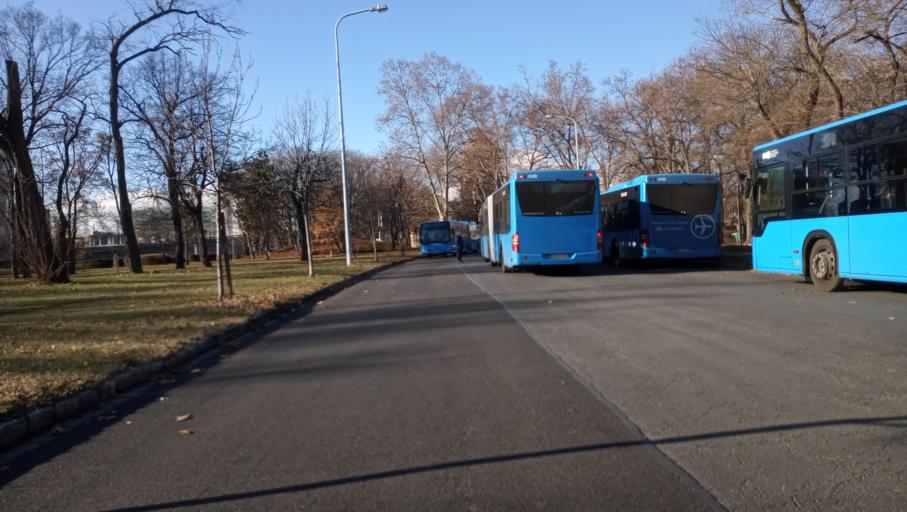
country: HU
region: Budapest
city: Budapest VIII. keruelet
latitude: 47.4750
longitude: 19.1031
